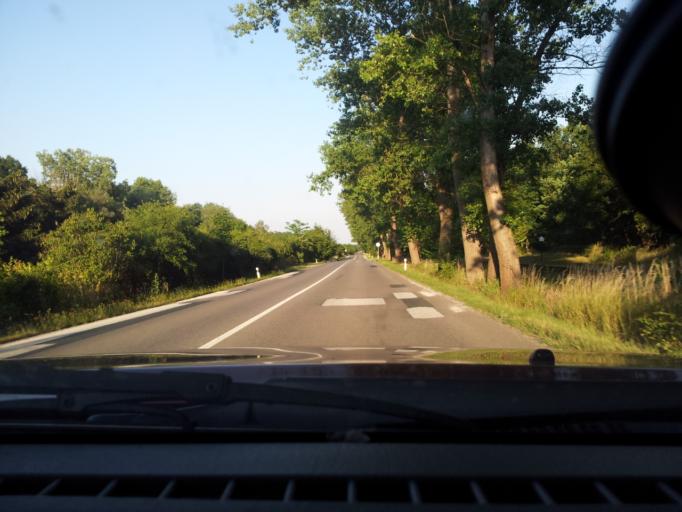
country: CZ
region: South Moravian
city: Dubnany
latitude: 48.8837
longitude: 17.0970
